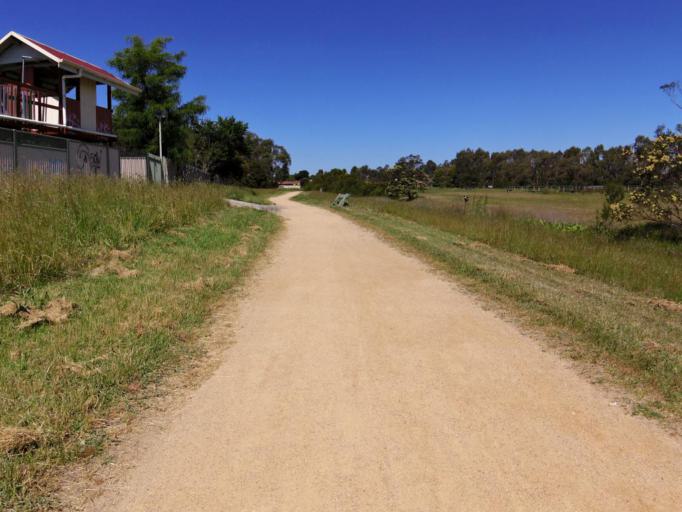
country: AU
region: Victoria
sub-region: Casey
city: Narre Warren South
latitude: -38.0363
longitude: 145.2733
